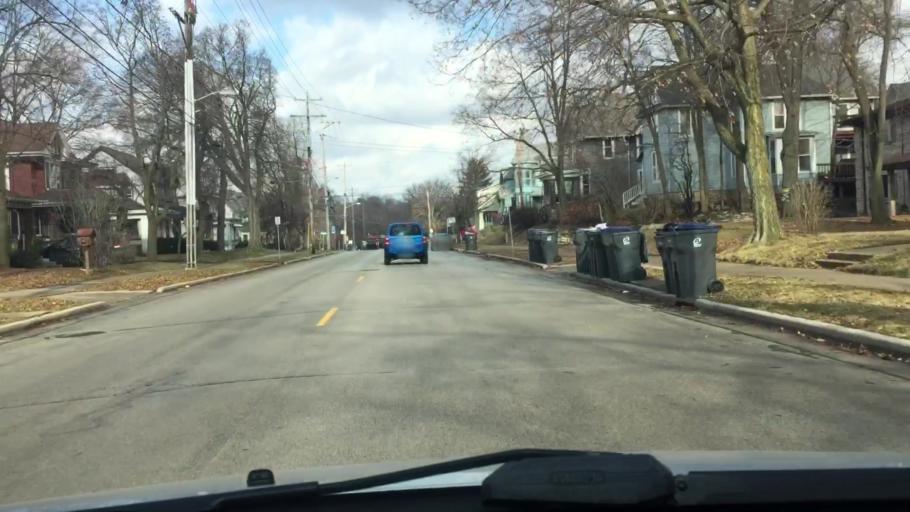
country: US
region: Wisconsin
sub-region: Waukesha County
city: Waukesha
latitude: 43.0078
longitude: -88.2366
